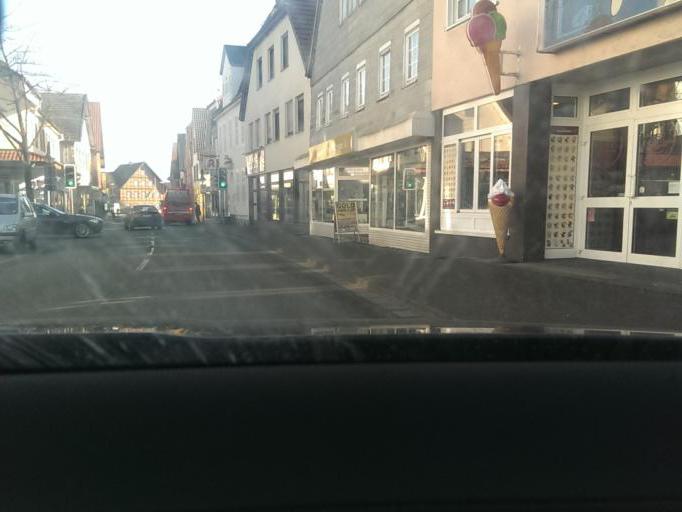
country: DE
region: North Rhine-Westphalia
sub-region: Regierungsbezirk Detmold
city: Delbruck
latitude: 51.7641
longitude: 8.5646
